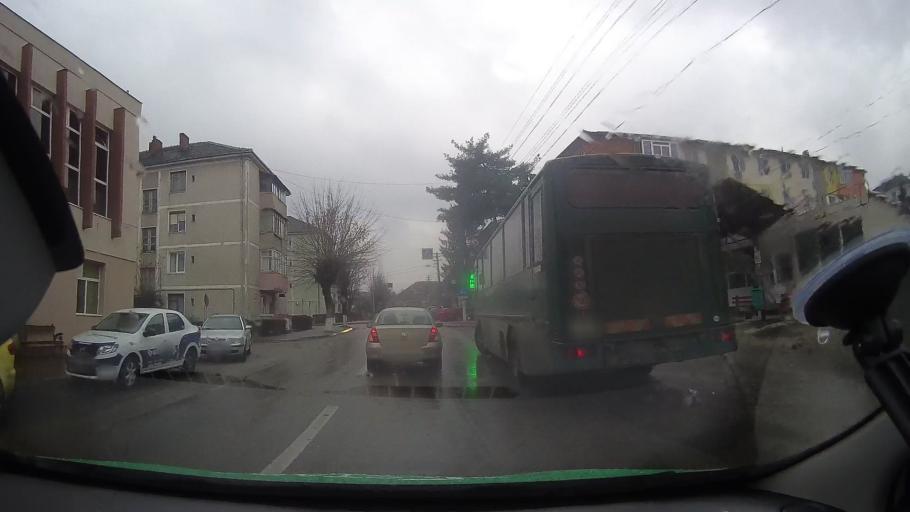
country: RO
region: Hunedoara
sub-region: Municipiul Brad
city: Brad
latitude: 46.1254
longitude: 22.7910
